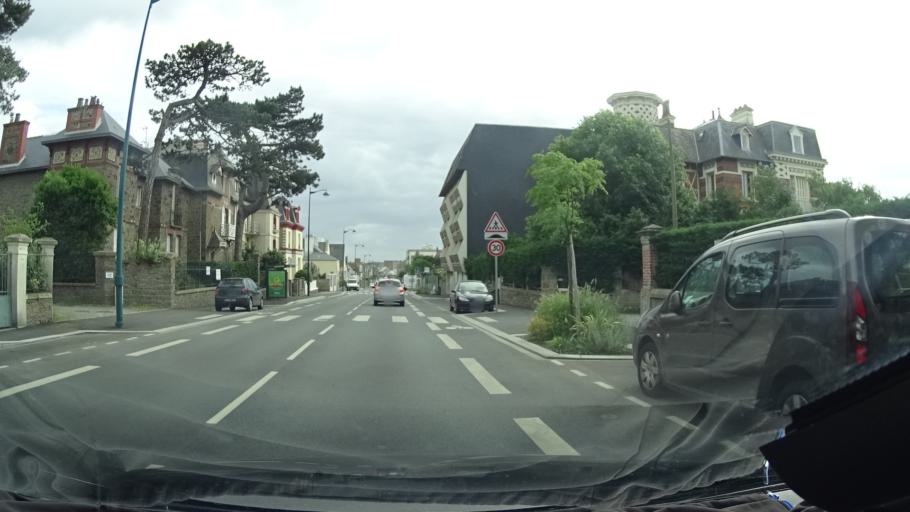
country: FR
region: Brittany
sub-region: Departement d'Ille-et-Vilaine
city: Saint-Malo
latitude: 48.6607
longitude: -1.9917
